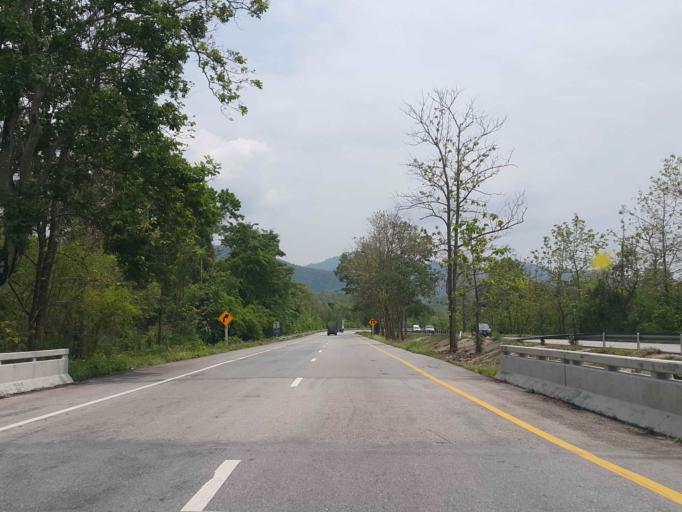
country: TH
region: Lampang
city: Sop Prap
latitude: 17.8049
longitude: 99.2666
